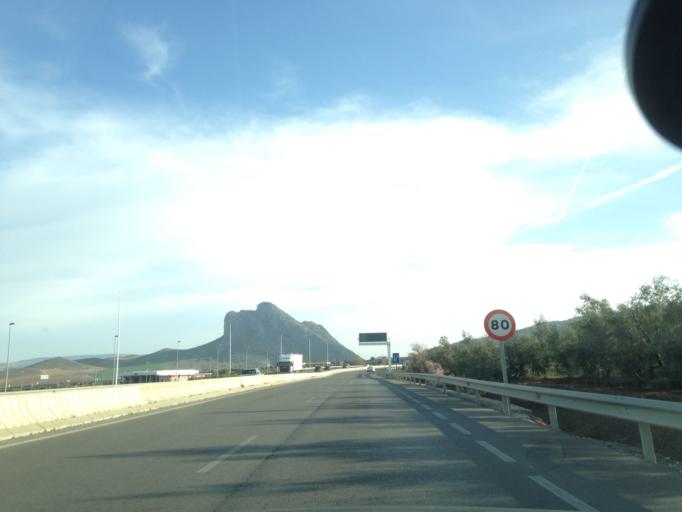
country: ES
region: Andalusia
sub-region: Provincia de Malaga
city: Antequera
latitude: 37.0421
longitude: -4.5154
